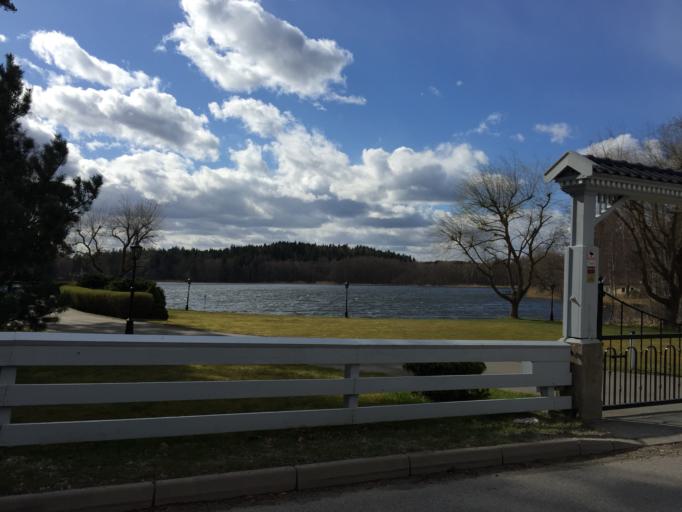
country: SE
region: Stockholm
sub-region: Botkyrka Kommun
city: Tumba
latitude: 59.1954
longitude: 17.8030
